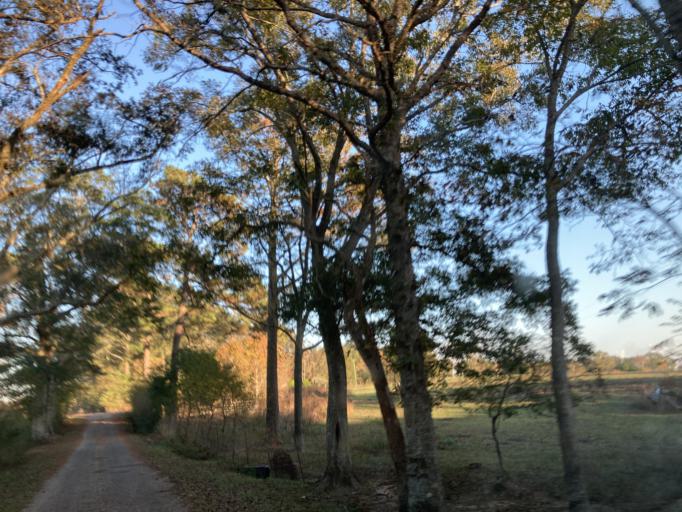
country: US
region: Mississippi
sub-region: Lamar County
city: Sumrall
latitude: 31.4010
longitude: -89.6159
